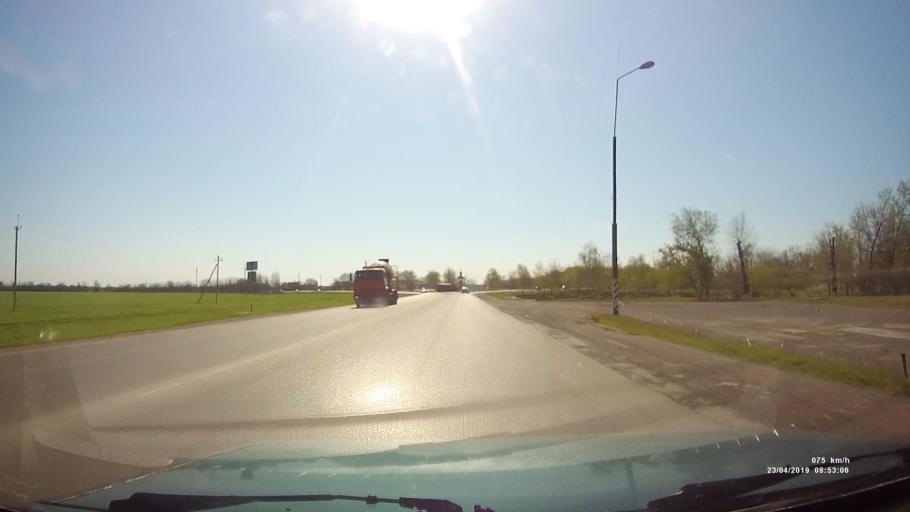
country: RU
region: Rostov
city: Sal'sk
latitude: 46.4767
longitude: 41.4708
